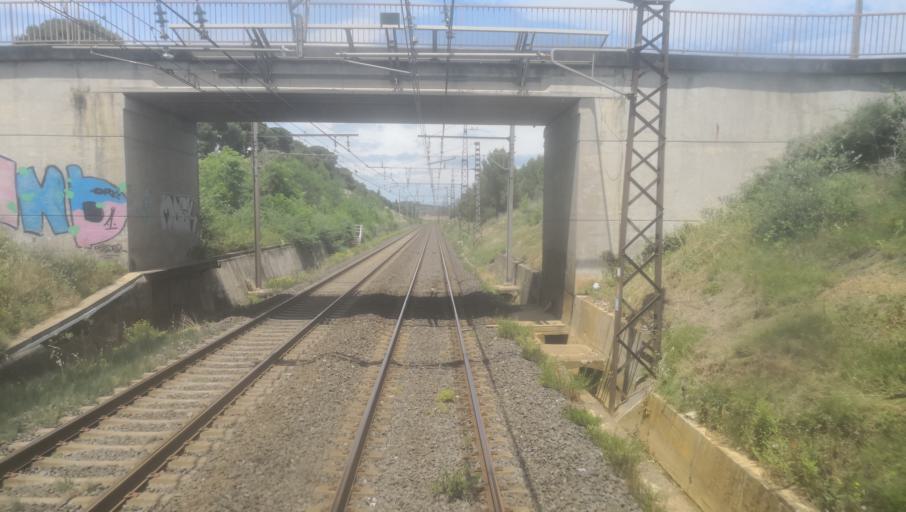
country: FR
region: Languedoc-Roussillon
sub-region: Departement de l'Aude
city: Marcorignan
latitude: 43.2009
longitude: 2.9367
